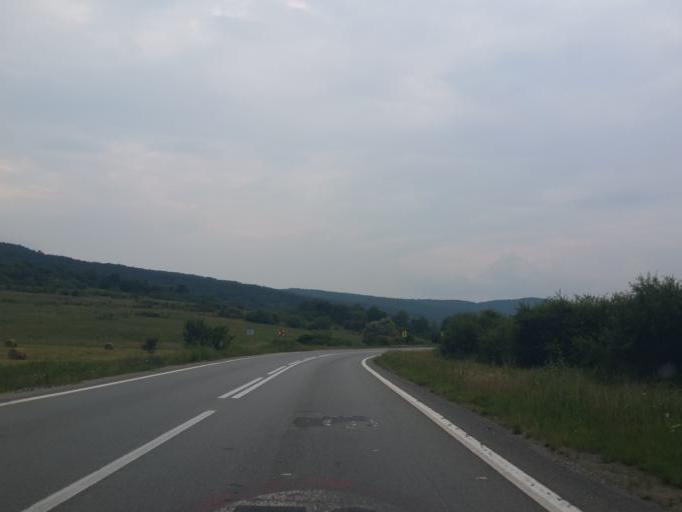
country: RO
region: Salaj
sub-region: Comuna Zimbor
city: Zimbor
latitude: 46.9680
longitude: 23.2804
